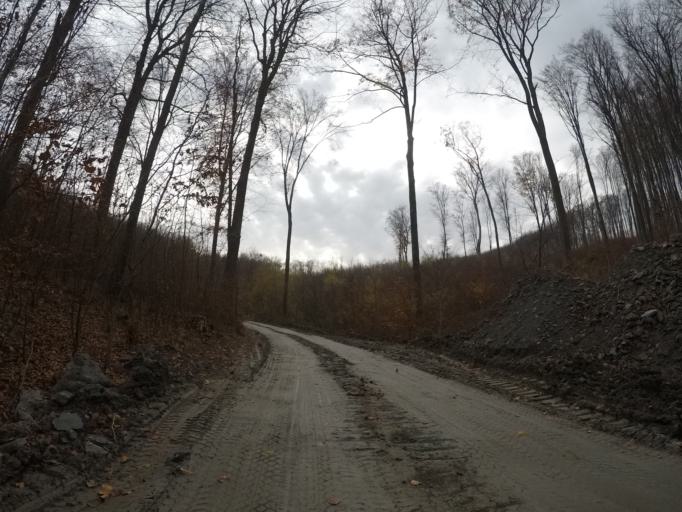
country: SK
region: Presovsky
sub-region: Okres Presov
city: Presov
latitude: 48.9745
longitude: 21.2160
